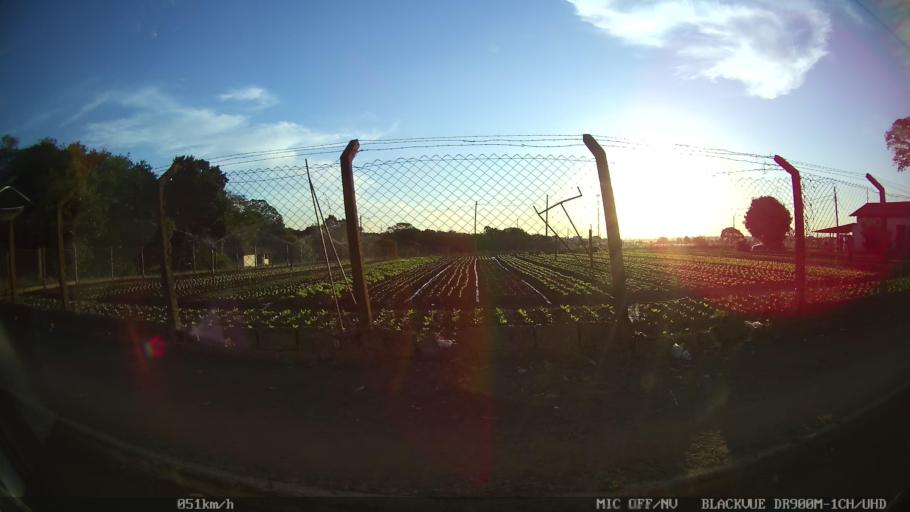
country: BR
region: Sao Paulo
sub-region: Franca
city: Franca
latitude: -20.4965
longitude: -47.4072
